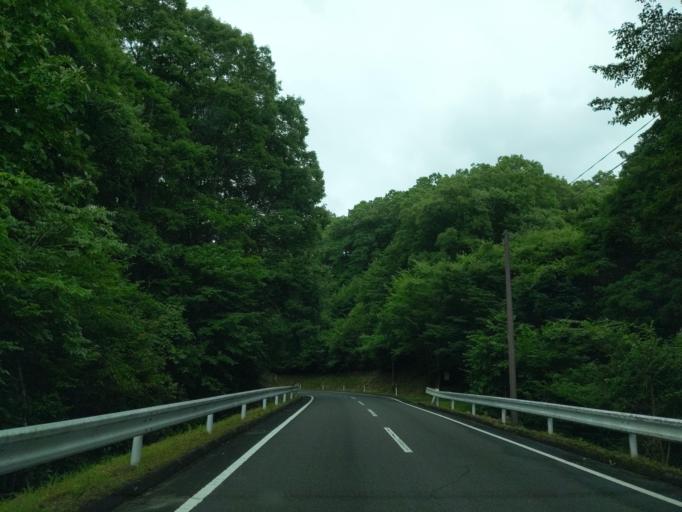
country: JP
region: Tochigi
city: Kuroiso
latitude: 37.2541
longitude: 140.0867
